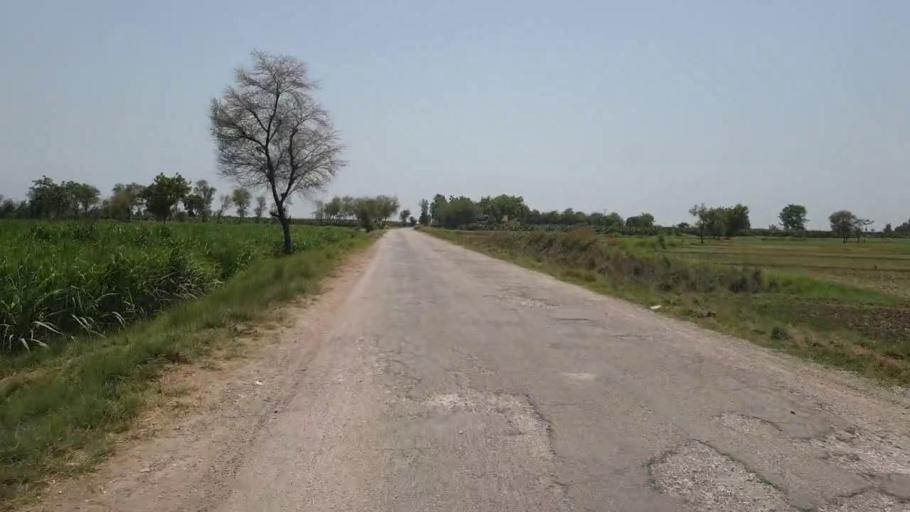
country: PK
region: Sindh
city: Daur
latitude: 26.3895
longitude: 68.1942
